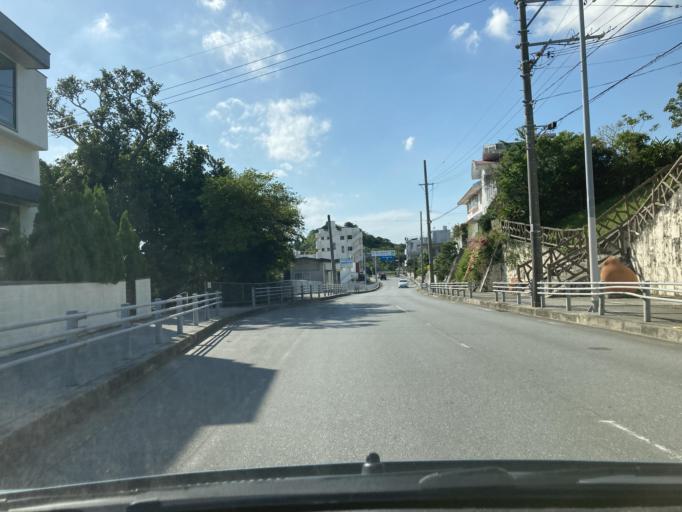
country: JP
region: Okinawa
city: Chatan
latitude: 26.2969
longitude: 127.7880
